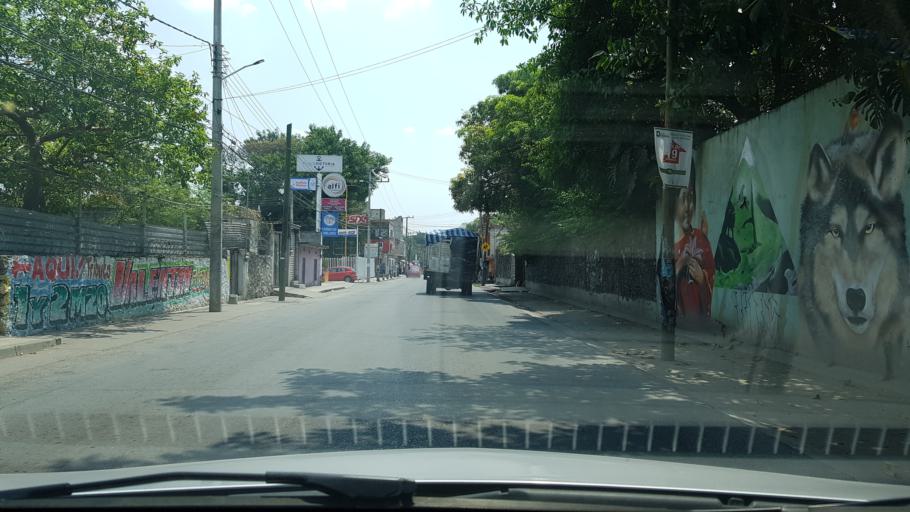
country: MX
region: Morelos
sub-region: Jiutepec
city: Jiutepec
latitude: 18.8781
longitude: -99.1762
